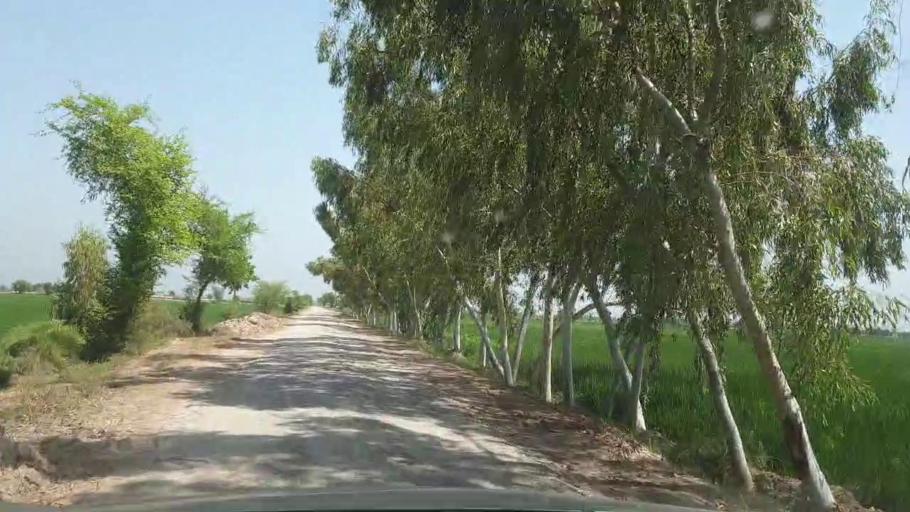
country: PK
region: Sindh
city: Warah
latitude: 27.5092
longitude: 67.7739
